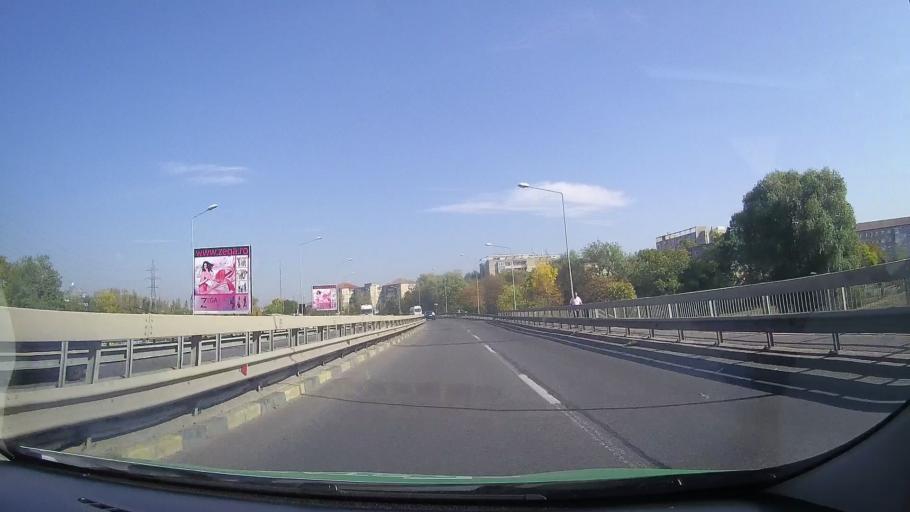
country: RO
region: Bihor
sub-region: Comuna Biharea
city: Oradea
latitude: 47.0719
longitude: 21.9056
